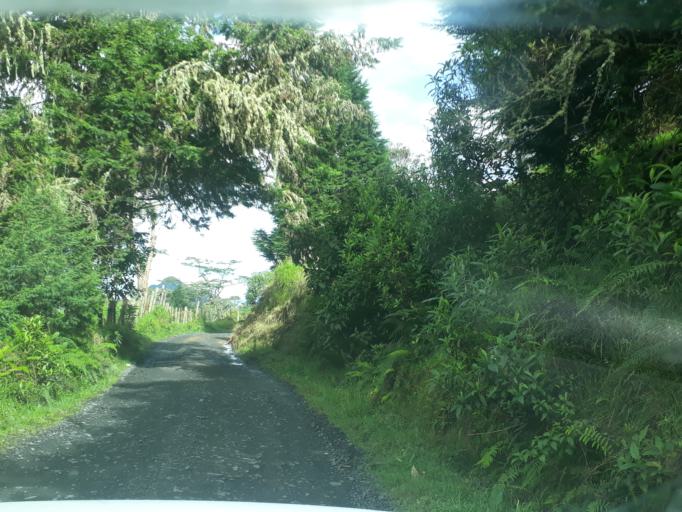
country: CO
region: Cundinamarca
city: La Mesa
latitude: 5.3323
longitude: -74.0557
